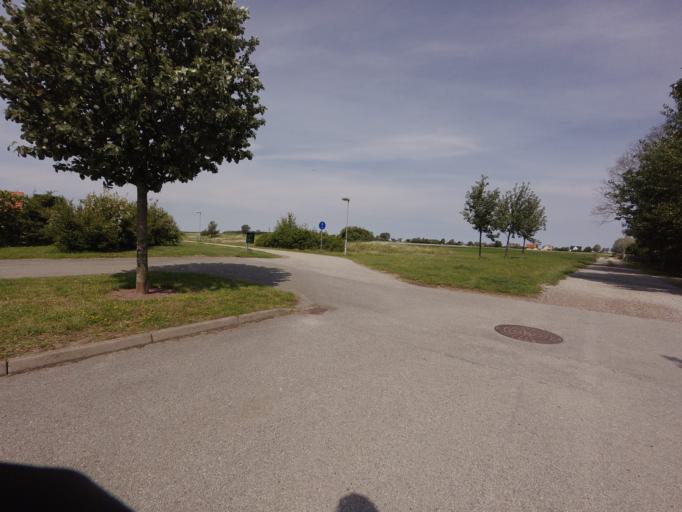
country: SE
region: Skane
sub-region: Malmo
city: Bunkeflostrand
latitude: 55.5311
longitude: 12.9291
